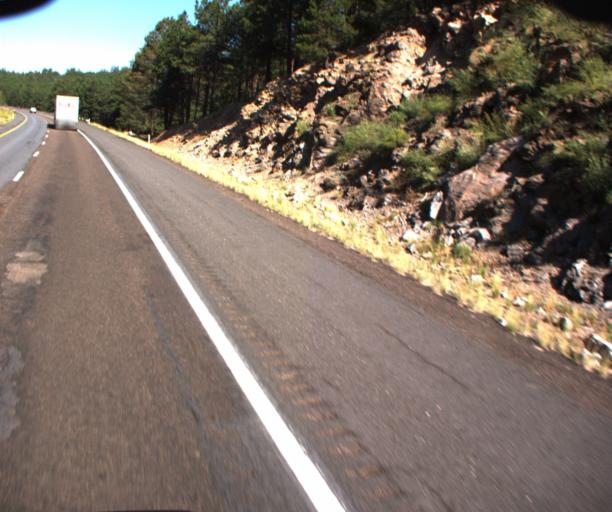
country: US
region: Arizona
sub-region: Coconino County
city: Parks
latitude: 35.2515
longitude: -111.8980
